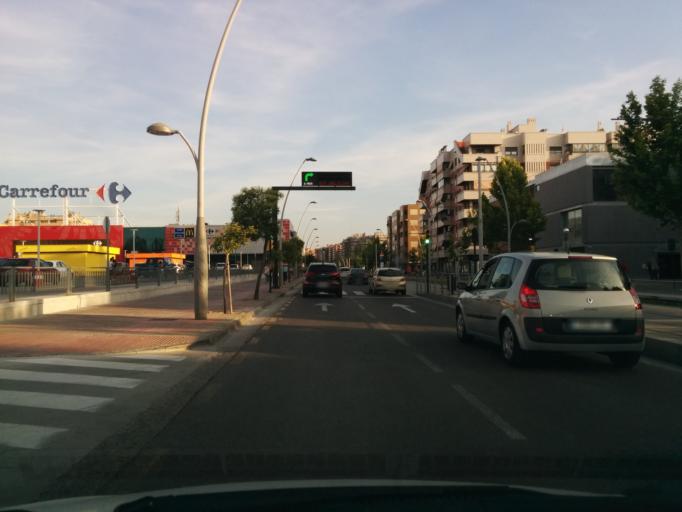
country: ES
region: Aragon
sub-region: Provincia de Zaragoza
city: Almozara
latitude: 41.6774
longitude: -0.8906
